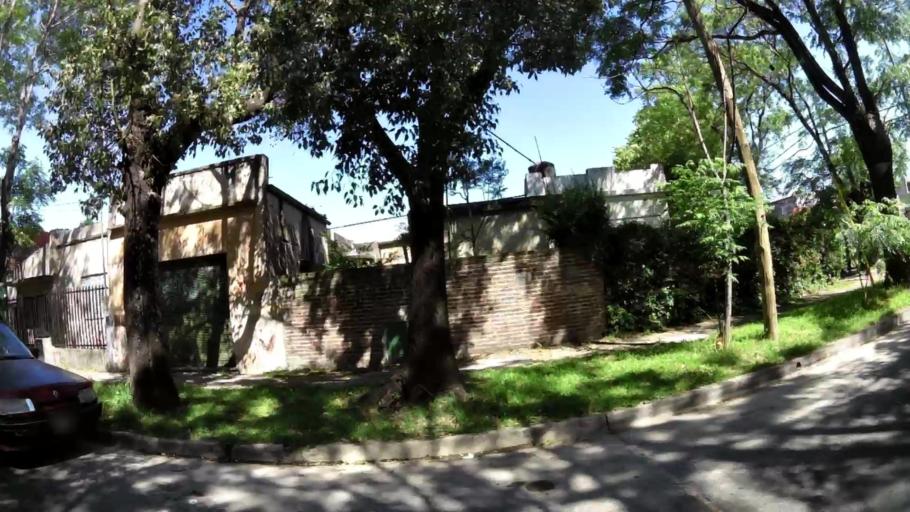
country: AR
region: Buenos Aires
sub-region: Partido de General San Martin
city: General San Martin
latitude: -34.5472
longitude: -58.5649
